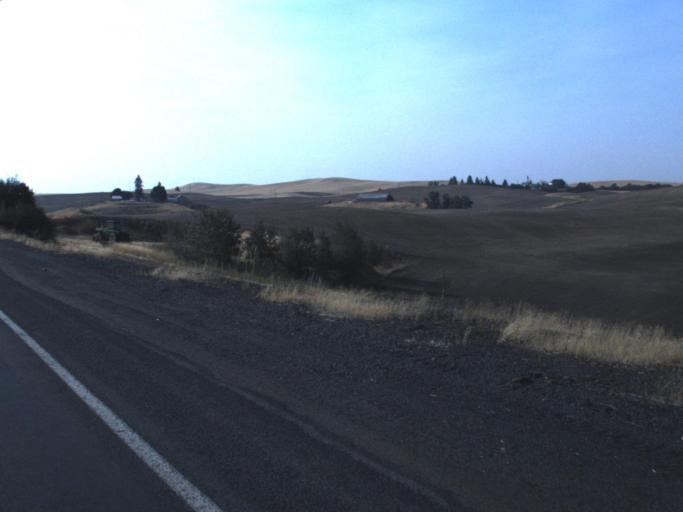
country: US
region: Idaho
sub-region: Benewah County
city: Plummer
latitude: 47.2372
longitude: -117.1194
